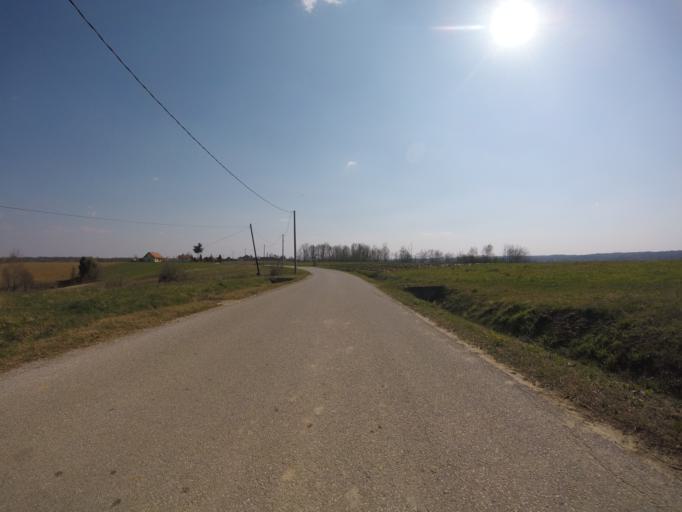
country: HR
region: Grad Zagreb
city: Strmec
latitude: 45.5242
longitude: 15.9234
